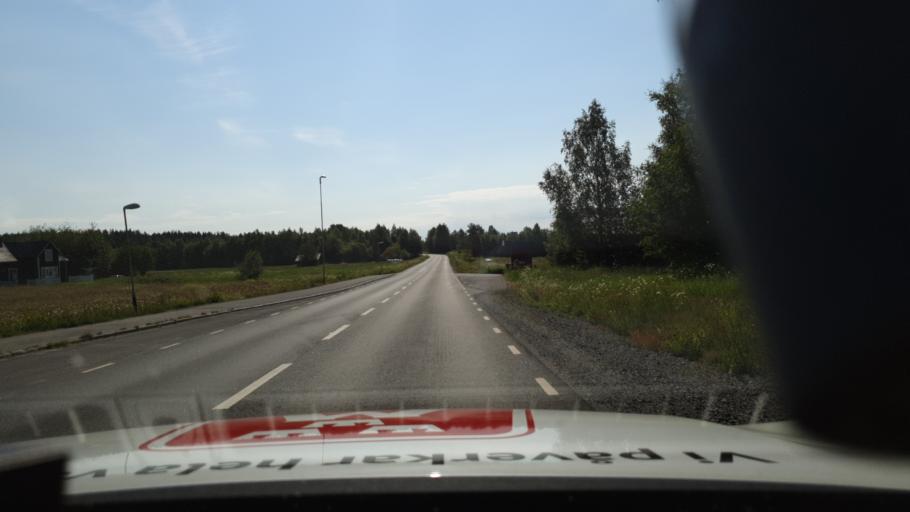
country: SE
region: Norrbotten
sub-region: Lulea Kommun
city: Gammelstad
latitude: 65.8057
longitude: 22.0314
